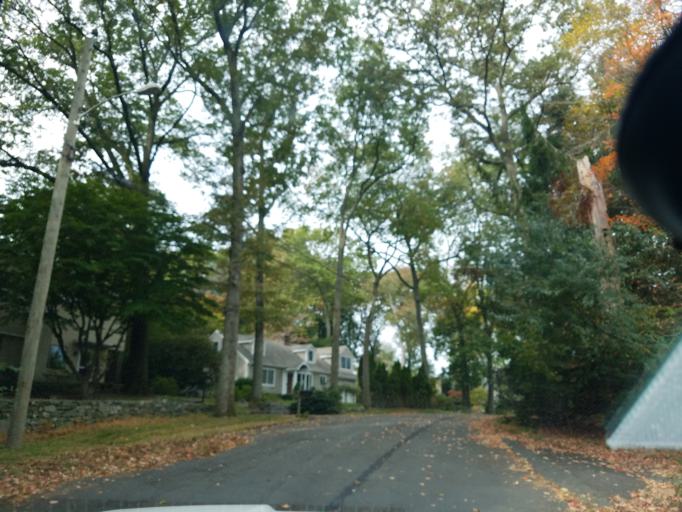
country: US
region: Connecticut
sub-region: Fairfield County
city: Stamford
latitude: 41.0753
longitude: -73.5454
